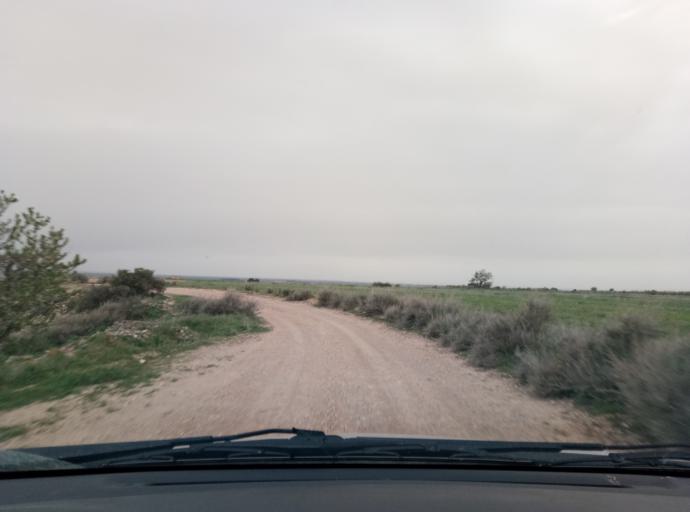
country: ES
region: Catalonia
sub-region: Provincia de Lleida
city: Verdu
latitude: 41.6119
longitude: 1.1034
